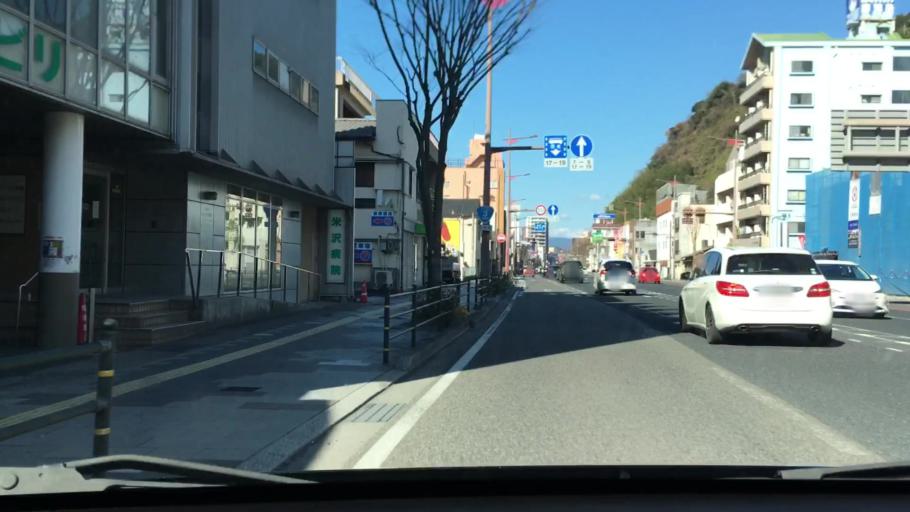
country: JP
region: Kagoshima
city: Kagoshima-shi
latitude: 31.5937
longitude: 130.5435
